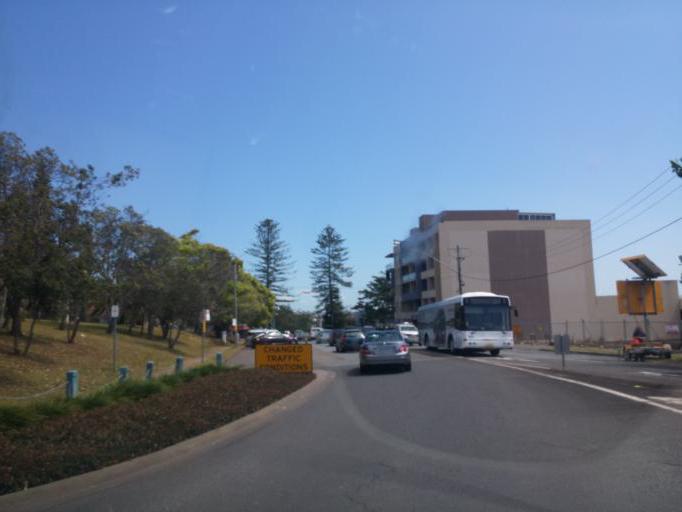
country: AU
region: New South Wales
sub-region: Port Macquarie-Hastings
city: Port Macquarie
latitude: -31.4312
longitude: 152.9110
